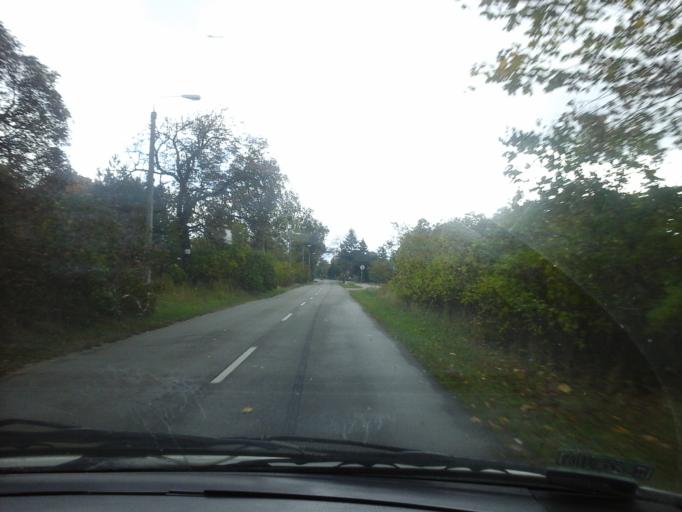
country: PL
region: Pomeranian Voivodeship
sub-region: Powiat gdanski
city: Cedry Wielkie
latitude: 54.3384
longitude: 18.9008
